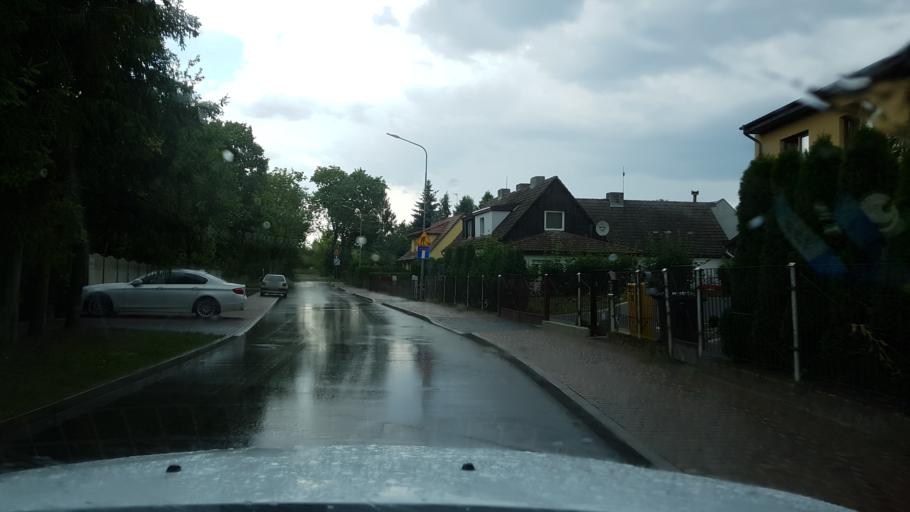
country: PL
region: West Pomeranian Voivodeship
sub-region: Powiat walecki
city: Walcz
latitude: 53.2831
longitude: 16.4662
